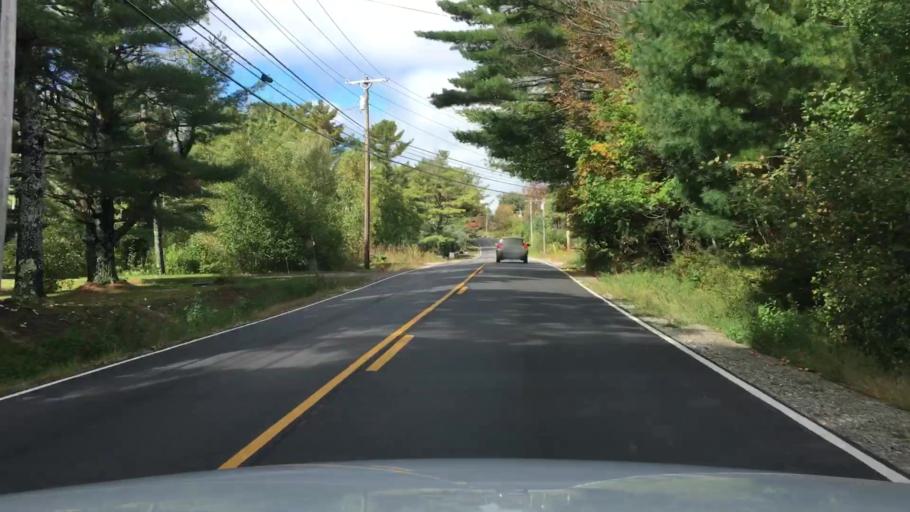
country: US
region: Maine
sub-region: Sagadahoc County
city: Topsham
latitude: 44.0136
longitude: -69.9096
